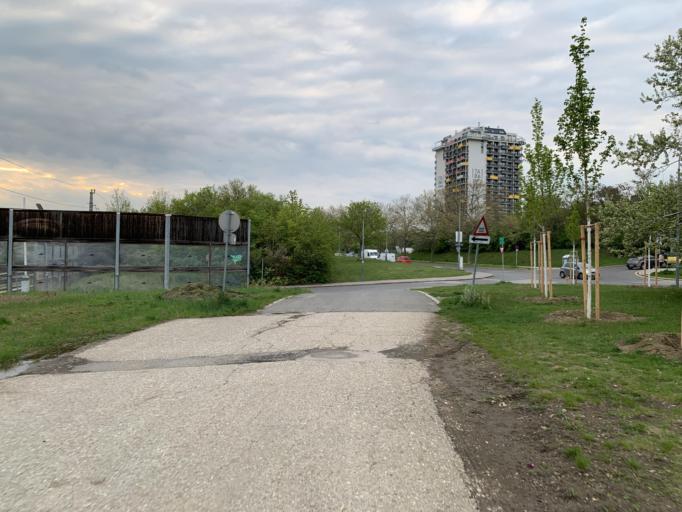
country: AT
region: Lower Austria
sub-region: Politischer Bezirk Wien-Umgebung
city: Leopoldsdorf
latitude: 48.1404
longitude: 16.4080
